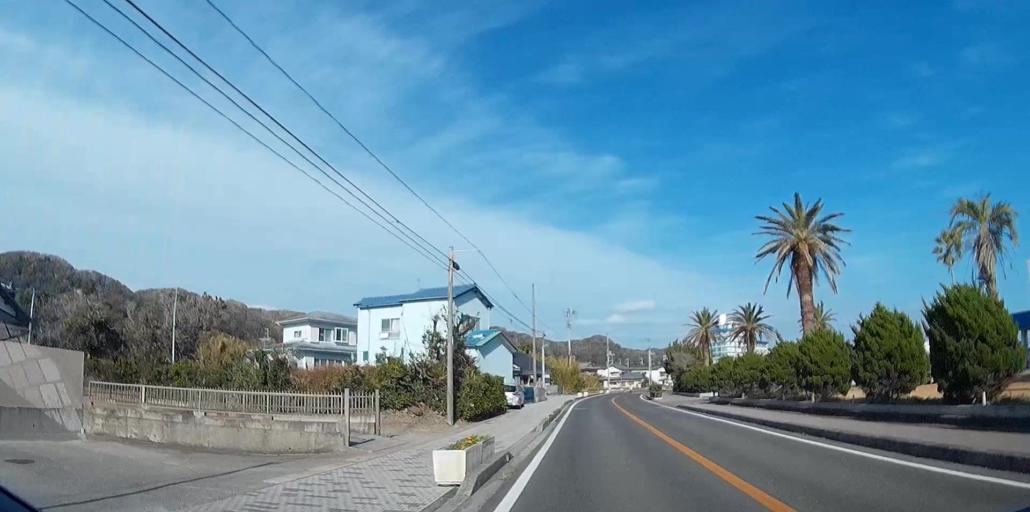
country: JP
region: Chiba
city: Tateyama
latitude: 34.9057
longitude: 139.8911
